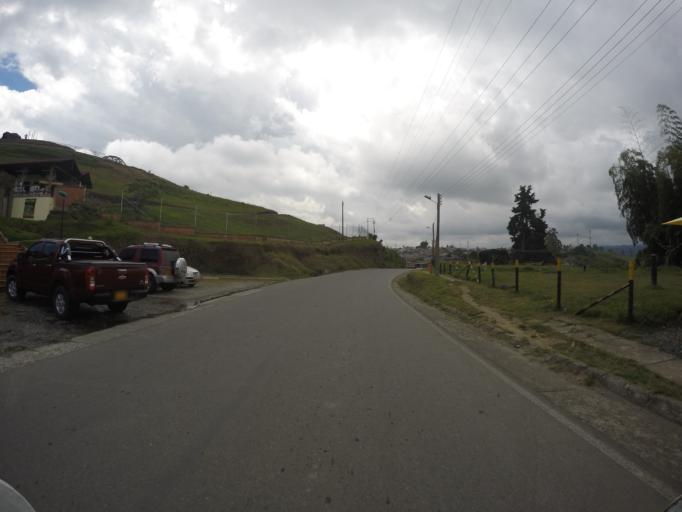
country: CO
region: Quindio
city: Filandia
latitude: 4.6684
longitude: -75.6648
